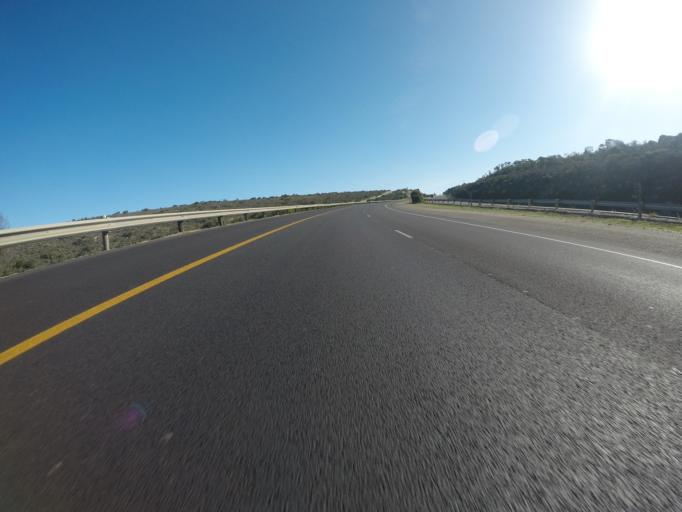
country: ZA
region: Western Cape
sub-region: Eden District Municipality
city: Mossel Bay
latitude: -34.1598
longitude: 22.0986
